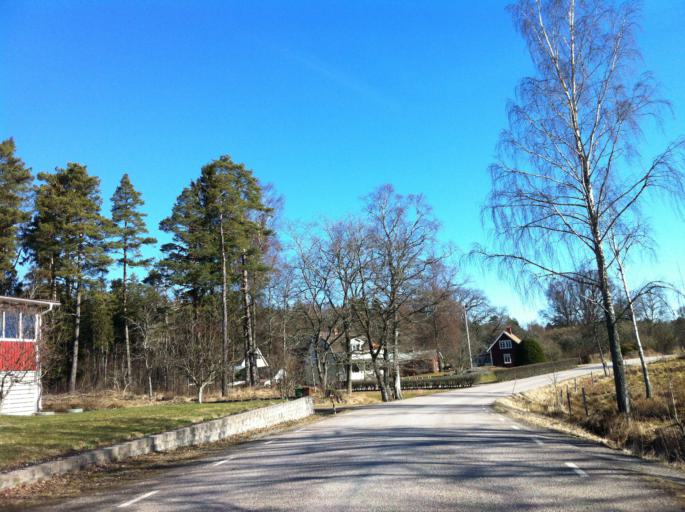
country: SE
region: Vaestra Goetaland
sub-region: Grastorps Kommun
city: Graestorp
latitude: 58.3996
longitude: 12.5707
